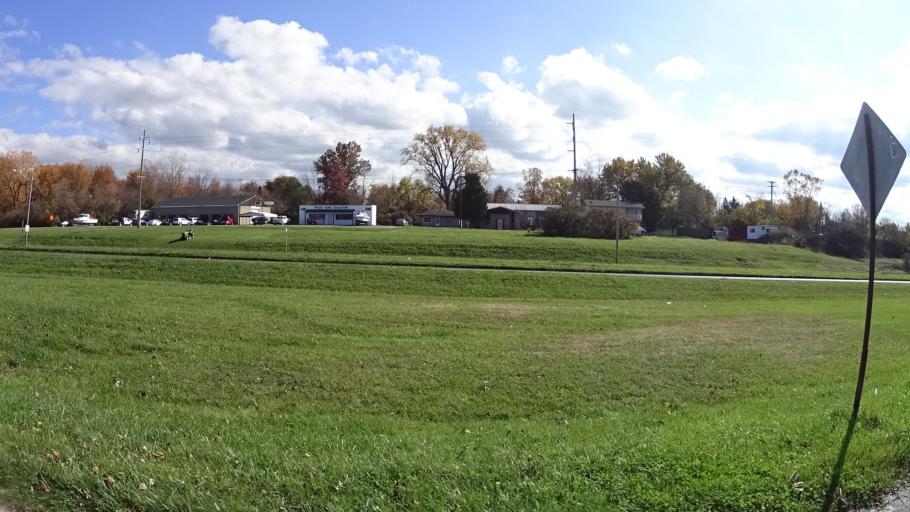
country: US
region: Ohio
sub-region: Lorain County
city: Lorain
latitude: 41.4495
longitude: -82.2216
